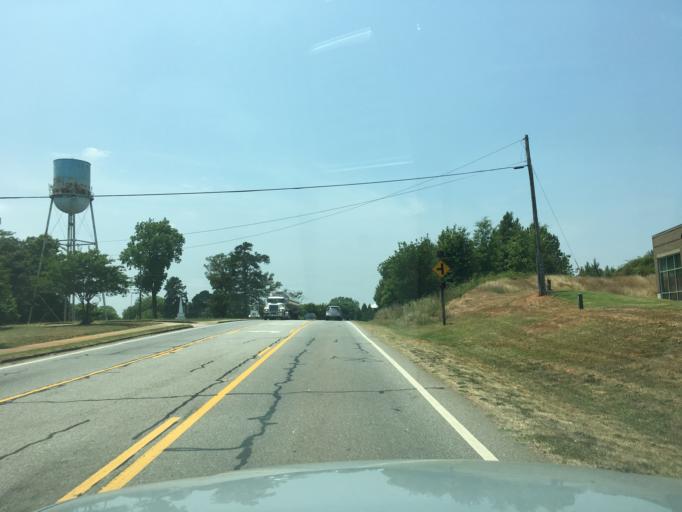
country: US
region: Georgia
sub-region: Hart County
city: Royston
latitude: 34.2847
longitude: -83.1454
